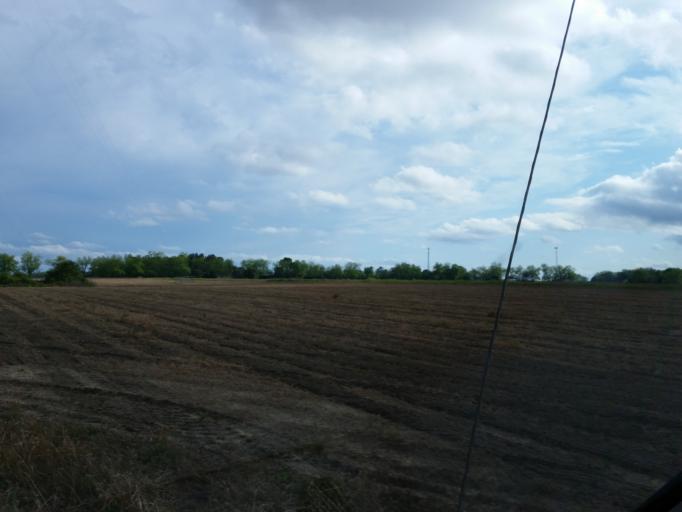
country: US
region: Georgia
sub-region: Dooly County
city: Unadilla
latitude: 32.1821
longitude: -83.7550
